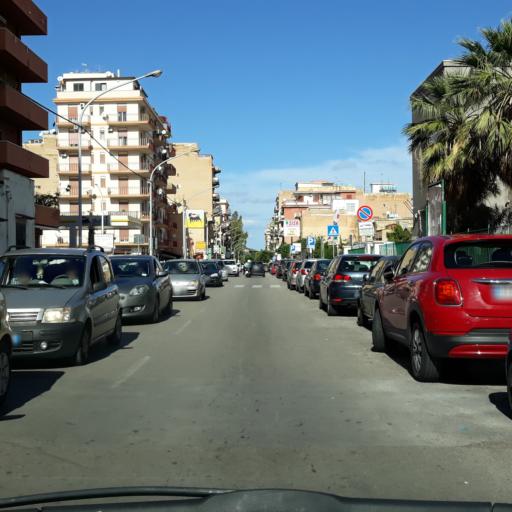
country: IT
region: Sicily
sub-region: Palermo
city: Palermo
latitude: 38.1505
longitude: 13.3707
